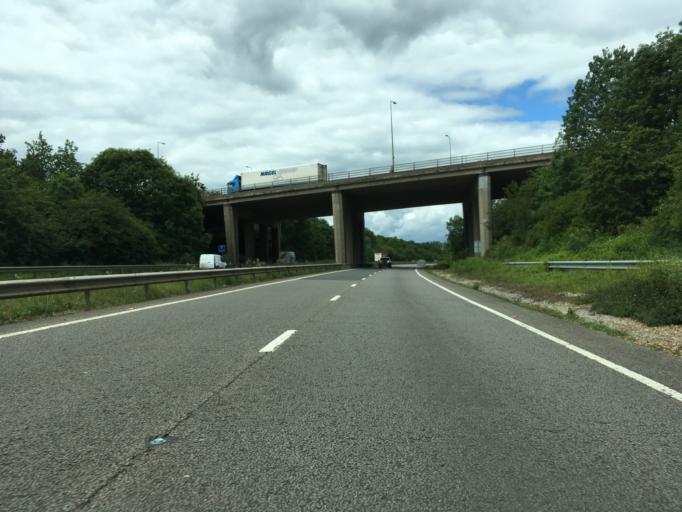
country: GB
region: England
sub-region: Buckinghamshire
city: Bletchley
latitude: 52.0129
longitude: -0.7489
